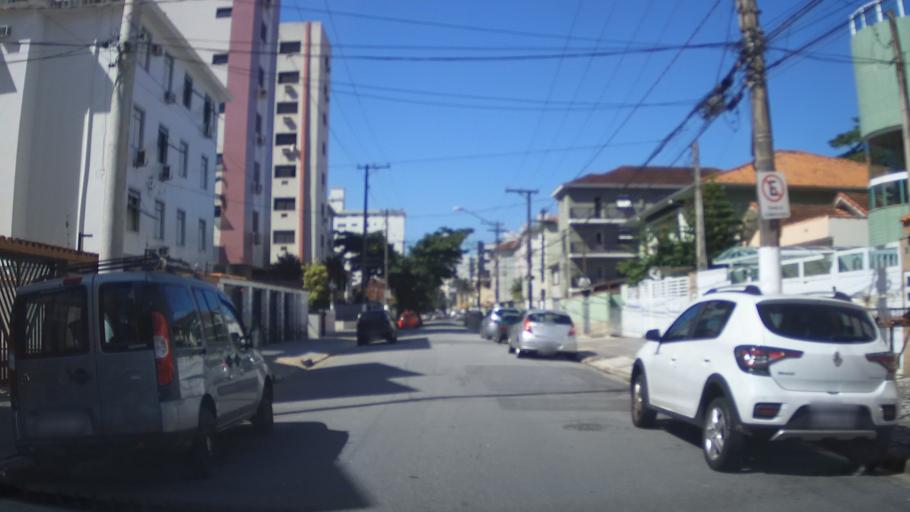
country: BR
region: Sao Paulo
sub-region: Santos
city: Santos
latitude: -23.9568
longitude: -46.3469
